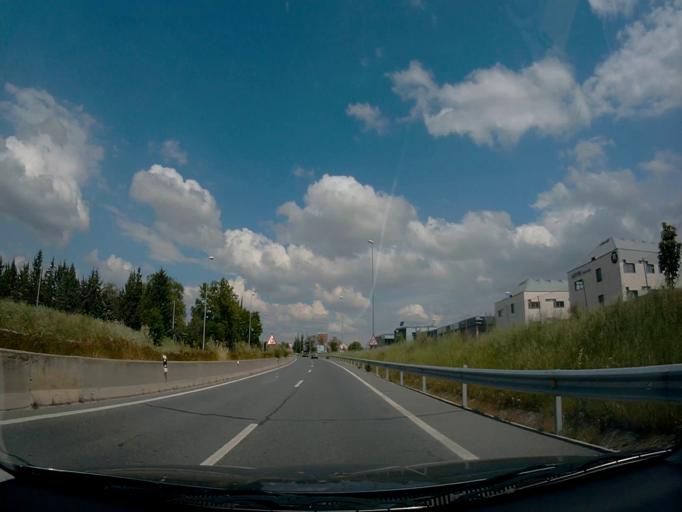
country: ES
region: Madrid
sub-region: Provincia de Madrid
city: Villaviciosa de Odon
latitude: 40.3512
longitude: -3.8948
